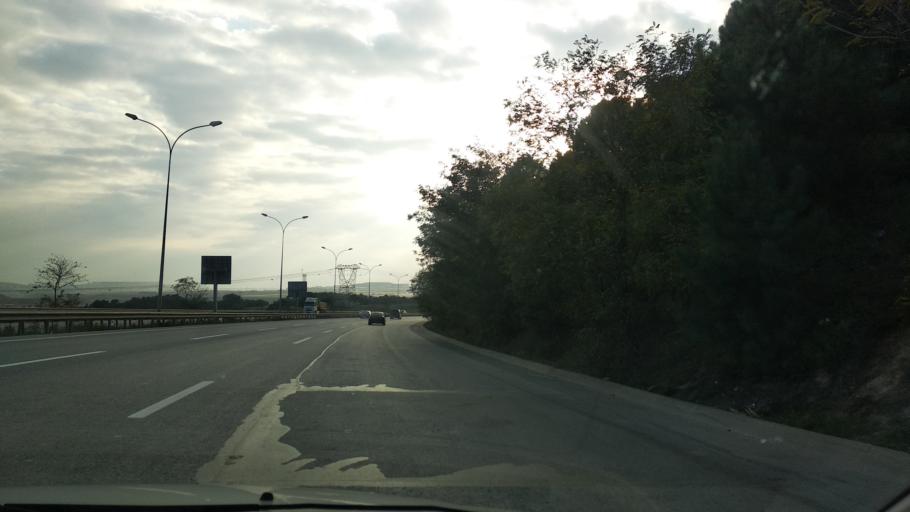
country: TR
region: Istanbul
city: Pendik
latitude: 40.9185
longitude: 29.3376
